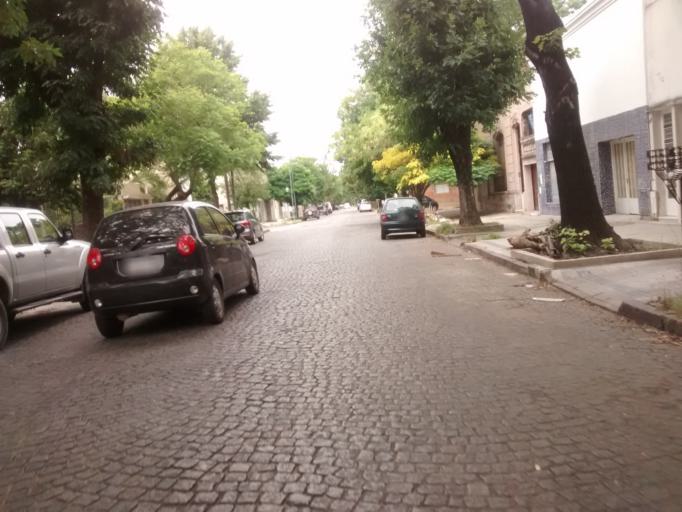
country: AR
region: Buenos Aires
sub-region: Partido de La Plata
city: La Plata
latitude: -34.9255
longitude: -57.9309
